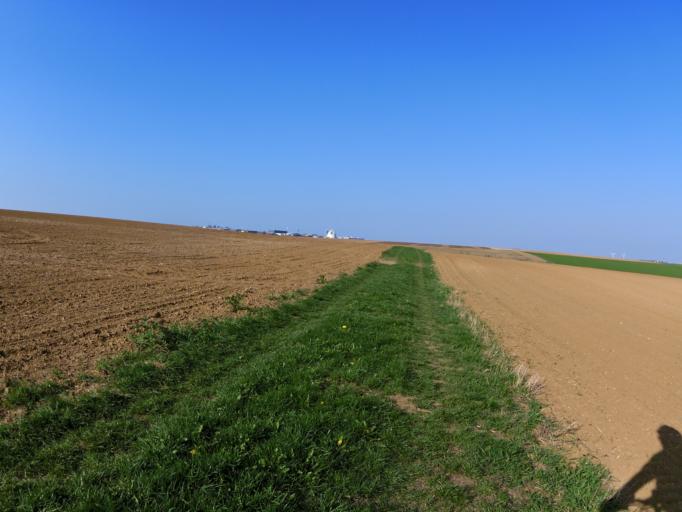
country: DE
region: Bavaria
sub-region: Regierungsbezirk Unterfranken
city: Theilheim
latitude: 49.7650
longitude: 10.0561
